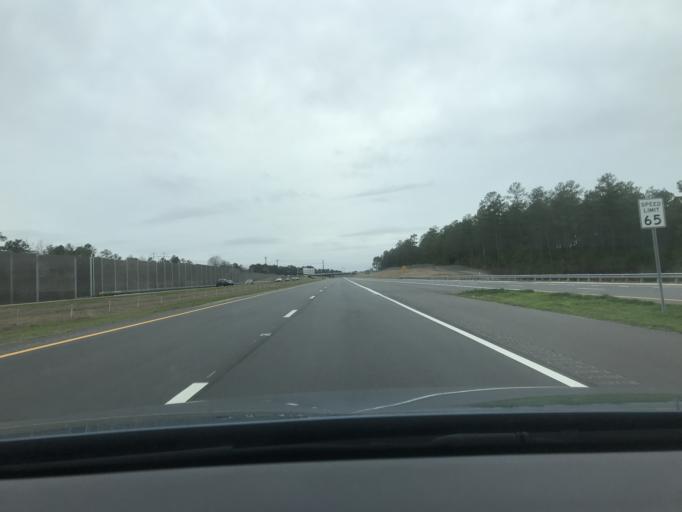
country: US
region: North Carolina
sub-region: Cumberland County
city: Fort Bragg
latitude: 35.1091
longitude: -78.9876
